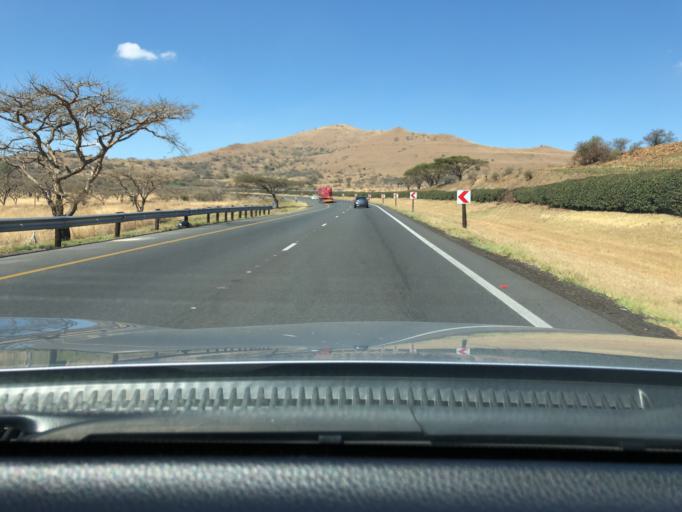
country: ZA
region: KwaZulu-Natal
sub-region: uThukela District Municipality
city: Estcourt
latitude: -29.0585
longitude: 29.9072
